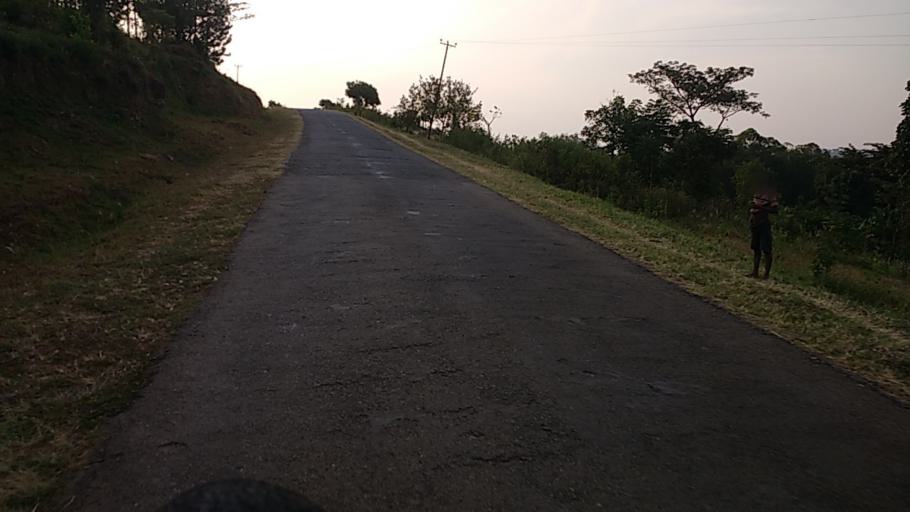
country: UG
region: Eastern Region
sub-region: Mbale District
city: Mbale
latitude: 1.0773
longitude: 34.2130
